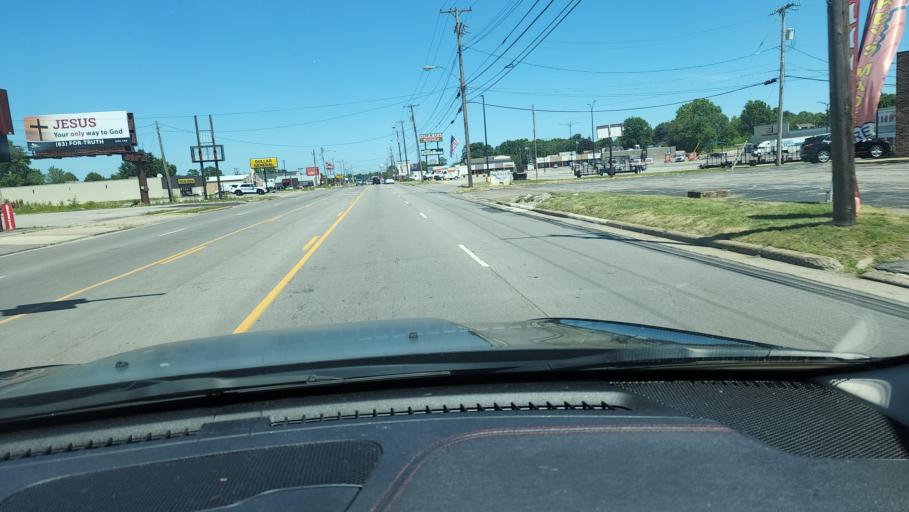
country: US
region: Ohio
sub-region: Mahoning County
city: Austintown
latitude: 41.1014
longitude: -80.7370
